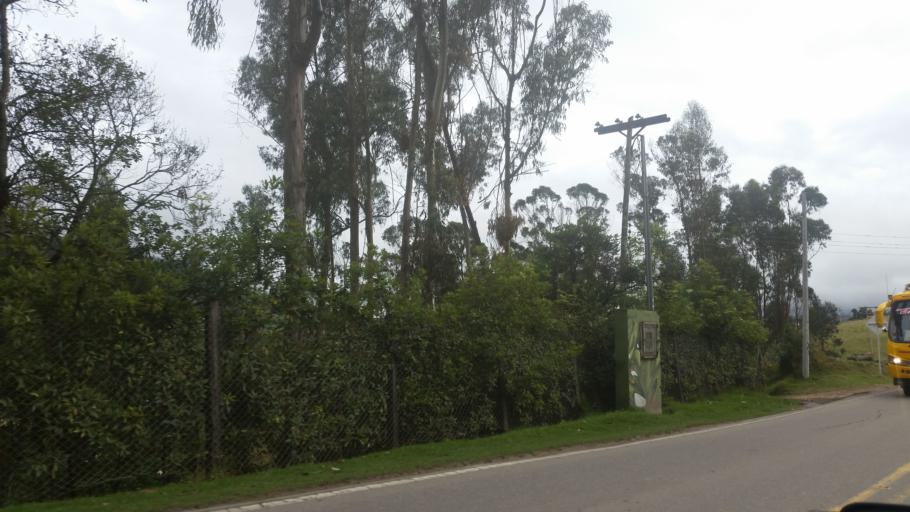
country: CO
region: Cundinamarca
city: La Calera
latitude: 4.7093
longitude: -73.9722
